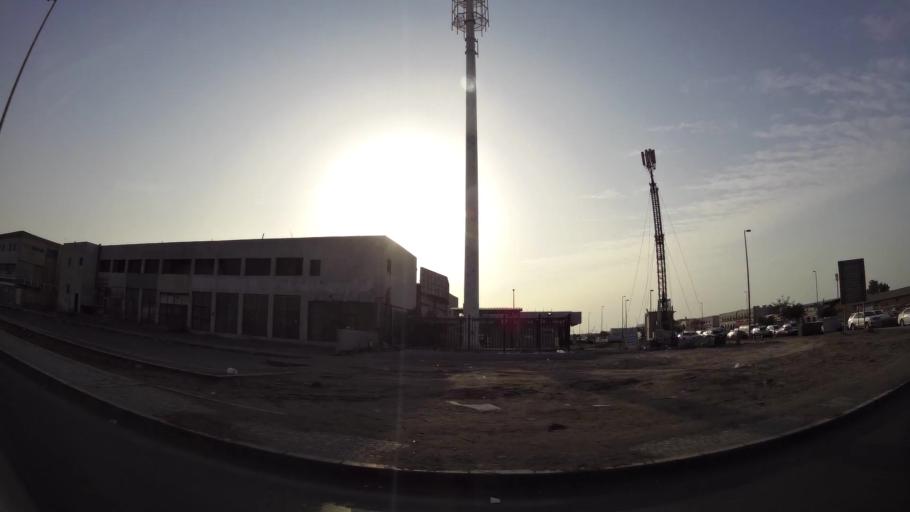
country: AE
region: Abu Dhabi
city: Abu Dhabi
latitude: 24.3683
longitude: 54.5111
